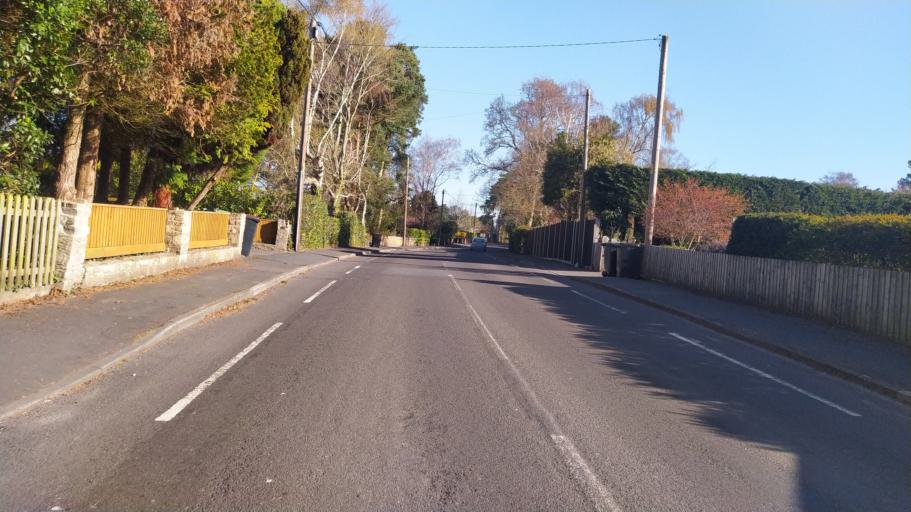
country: GB
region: England
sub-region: Dorset
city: St Leonards
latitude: 50.8361
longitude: -1.8390
